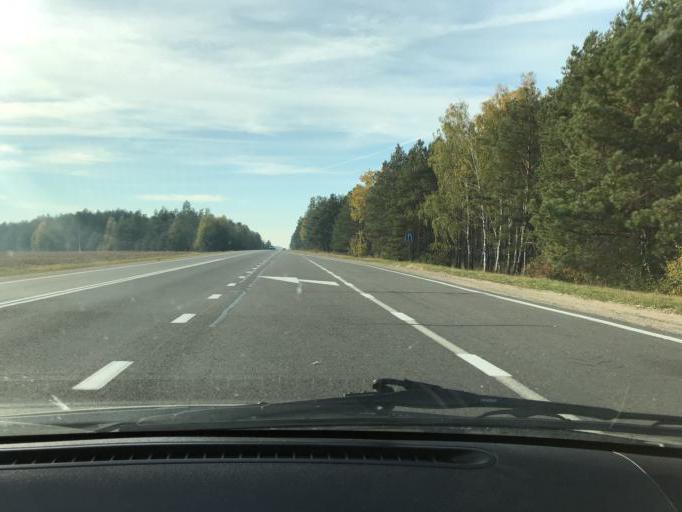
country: BY
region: Brest
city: Horad Pinsk
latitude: 52.1482
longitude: 25.8923
